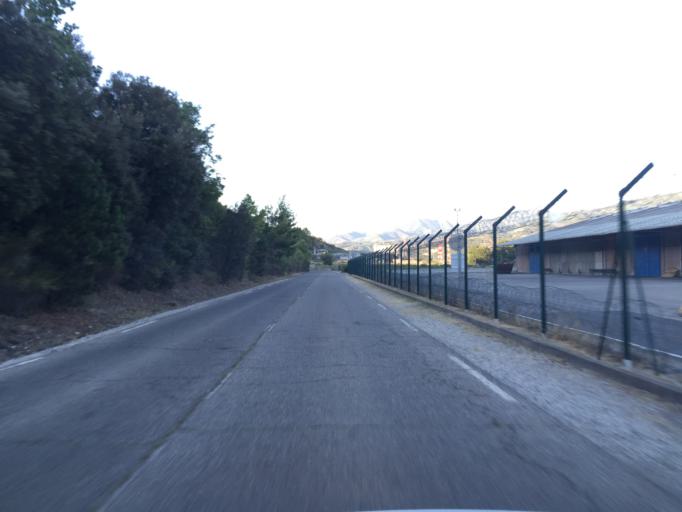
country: FR
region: Provence-Alpes-Cote d'Azur
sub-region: Departement des Alpes-de-Haute-Provence
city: Malijai
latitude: 44.0700
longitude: 6.0000
